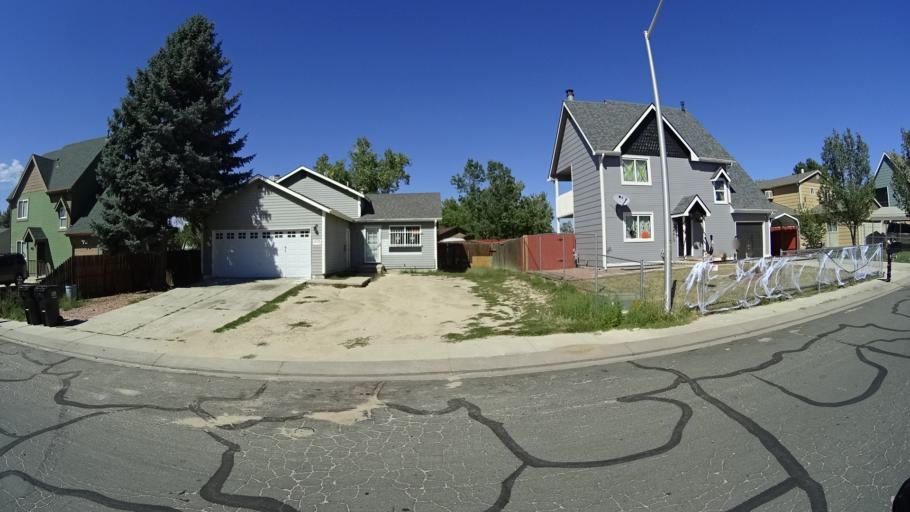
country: US
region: Colorado
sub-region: El Paso County
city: Stratmoor
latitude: 38.7840
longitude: -104.7456
